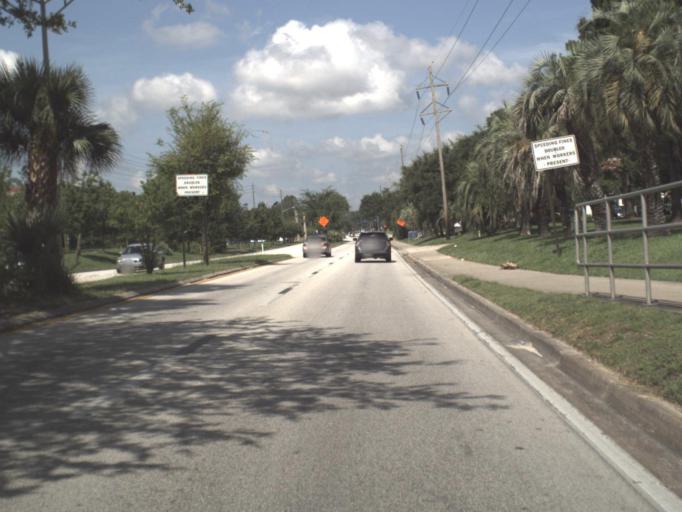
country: US
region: Florida
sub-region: Alachua County
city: Gainesville
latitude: 29.6379
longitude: -82.3471
